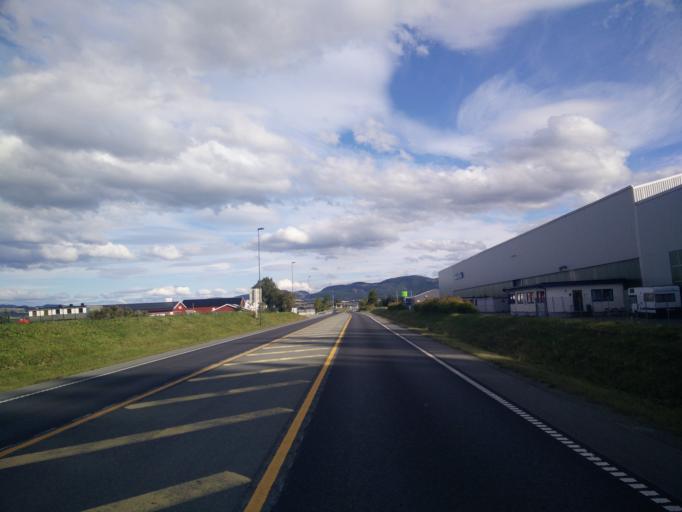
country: NO
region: Sor-Trondelag
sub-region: Melhus
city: Melhus
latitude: 63.3242
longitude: 10.2365
